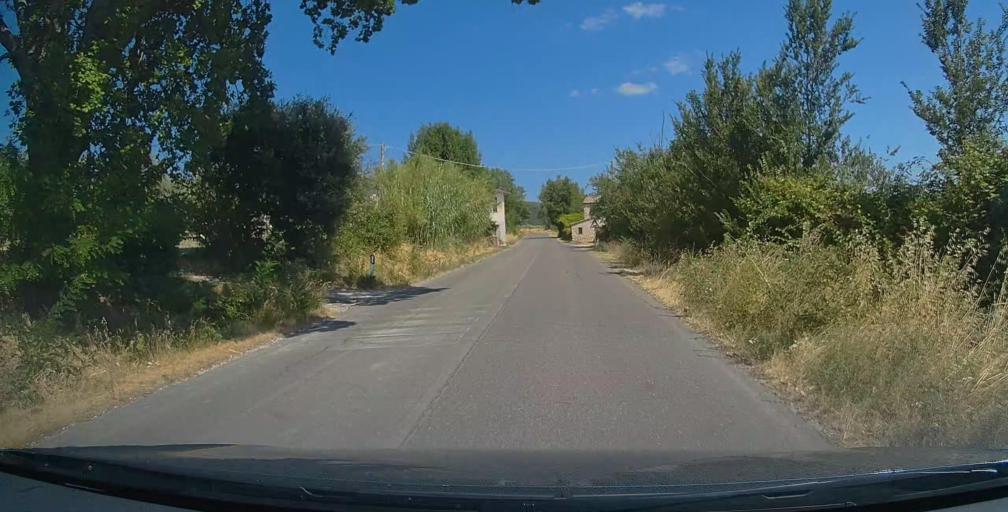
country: IT
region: Umbria
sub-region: Provincia di Terni
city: Calvi dell'Umbria
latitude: 42.4139
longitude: 12.5476
